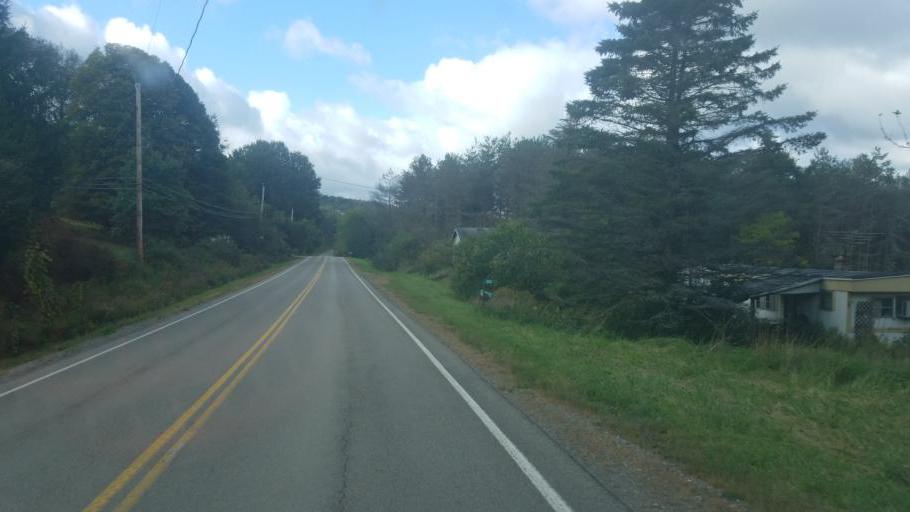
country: US
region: New York
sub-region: Allegany County
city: Cuba
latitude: 42.1478
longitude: -78.3056
